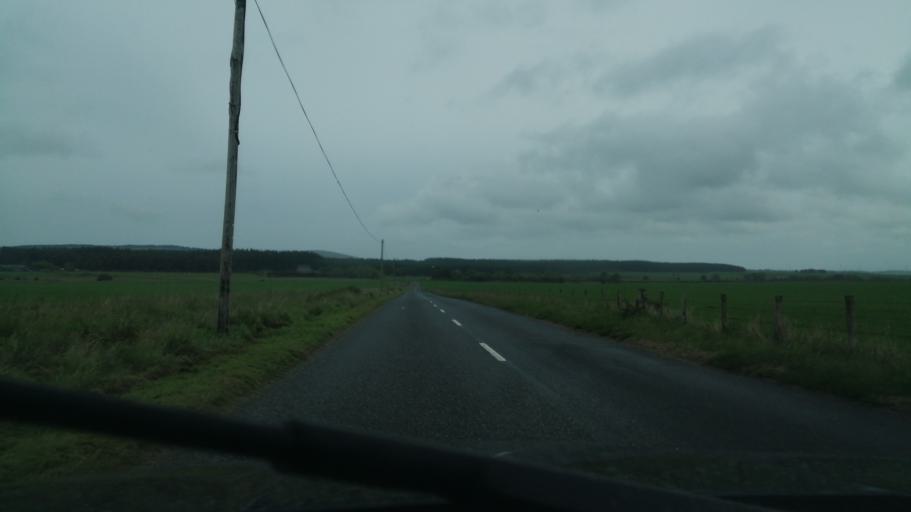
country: GB
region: Scotland
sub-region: Aberdeenshire
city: Portsoy
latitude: 57.6132
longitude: -2.7236
